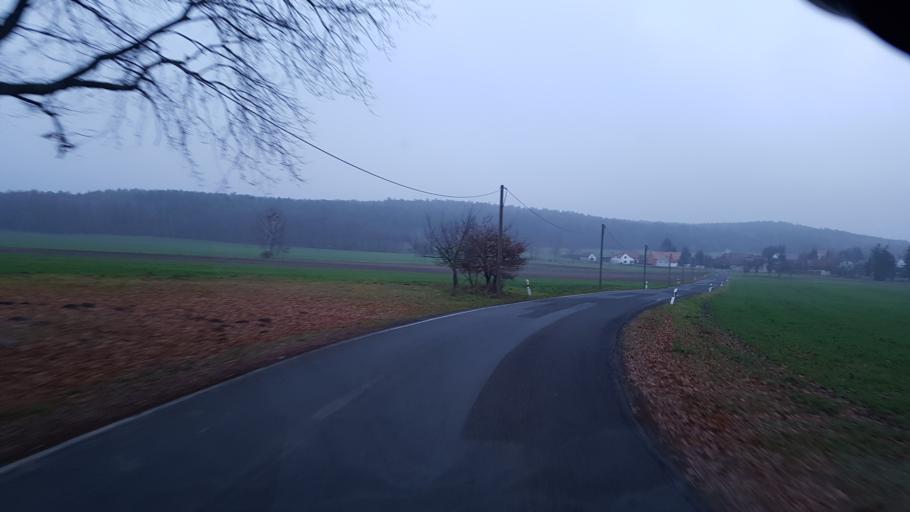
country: DE
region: Brandenburg
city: Bronkow
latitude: 51.6894
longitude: 13.9616
